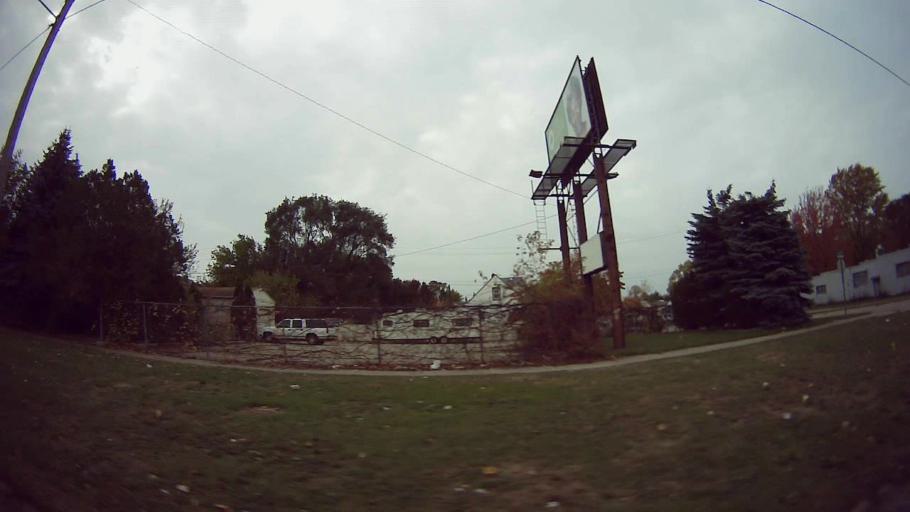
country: US
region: Michigan
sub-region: Oakland County
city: Hazel Park
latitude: 42.4493
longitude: -83.0835
